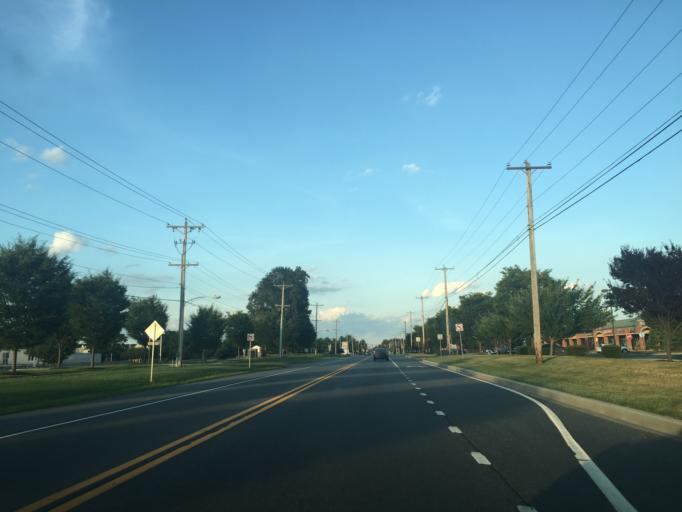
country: US
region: Delaware
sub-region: New Castle County
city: Middletown
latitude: 39.4502
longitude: -75.7058
